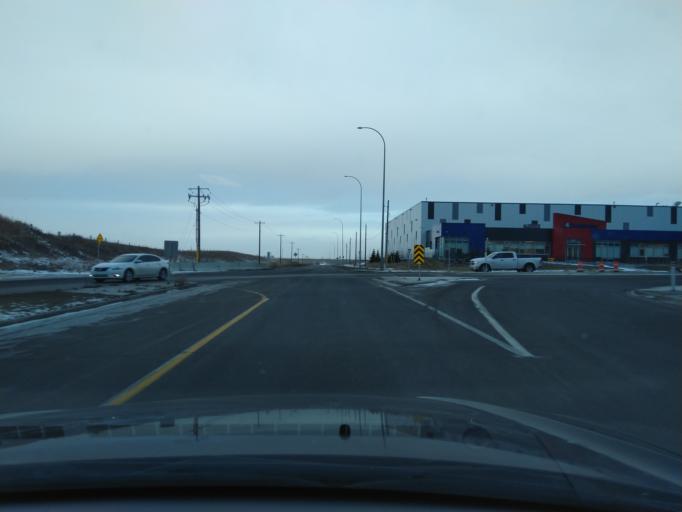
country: CA
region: Alberta
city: Calgary
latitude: 51.1612
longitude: -114.0249
